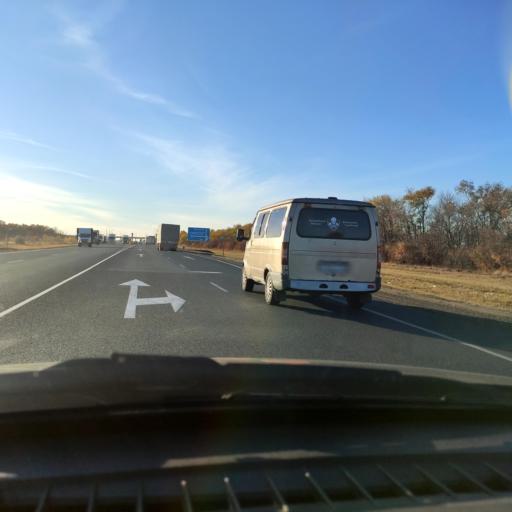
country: RU
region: Samara
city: Varlamovo
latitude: 53.1965
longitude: 48.3055
